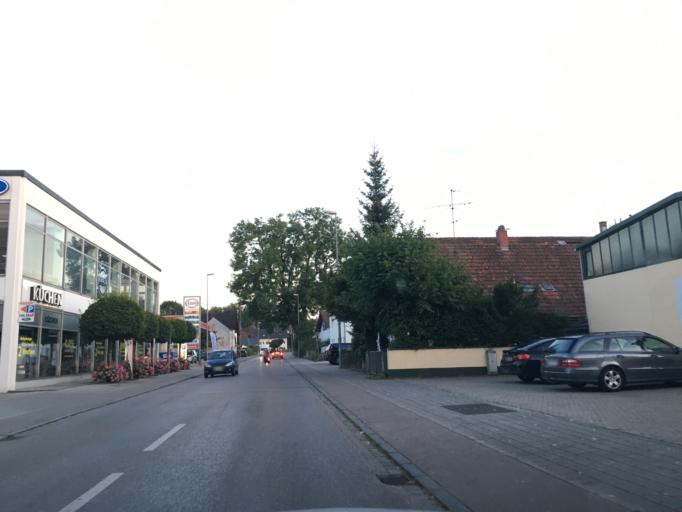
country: DE
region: Bavaria
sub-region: Upper Bavaria
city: Erding
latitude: 48.3019
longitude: 11.9003
